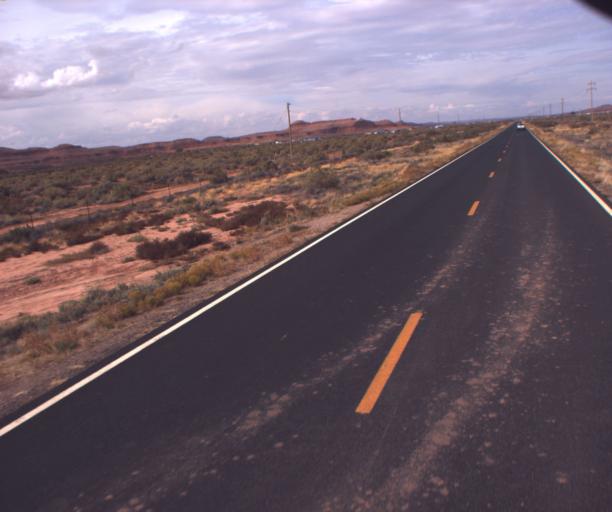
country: US
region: Arizona
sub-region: Apache County
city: Many Farms
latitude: 36.6865
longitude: -109.6069
